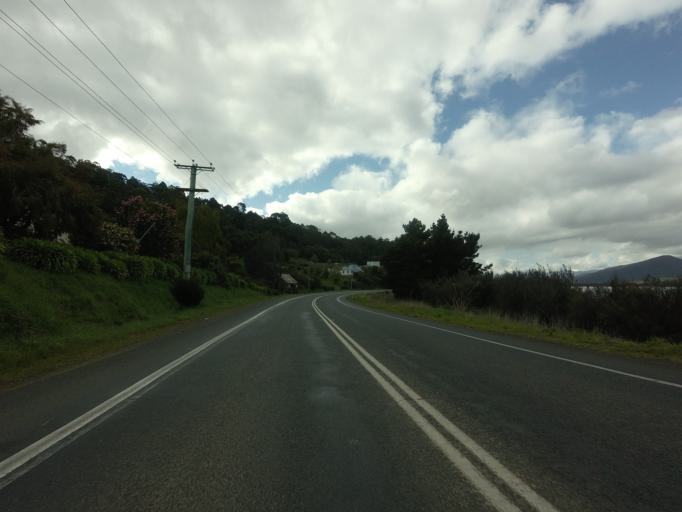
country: AU
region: Tasmania
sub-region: Huon Valley
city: Franklin
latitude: -43.1062
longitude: 147.0003
